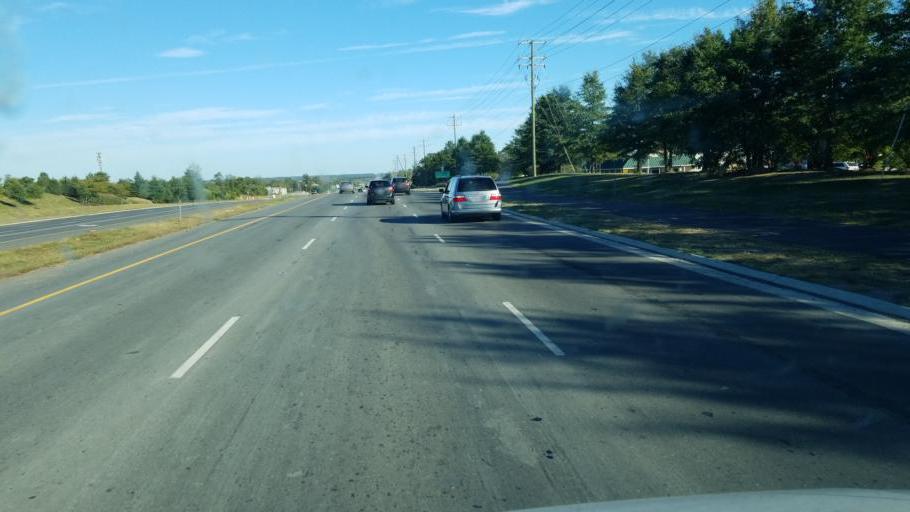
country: US
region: Virginia
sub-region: Loudoun County
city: South Riding
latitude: 38.9204
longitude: -77.4966
